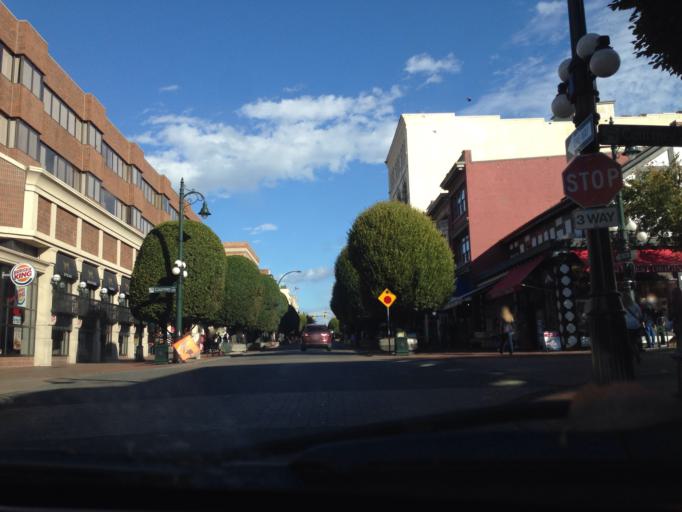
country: CA
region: British Columbia
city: Victoria
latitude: 48.4233
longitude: -123.3682
